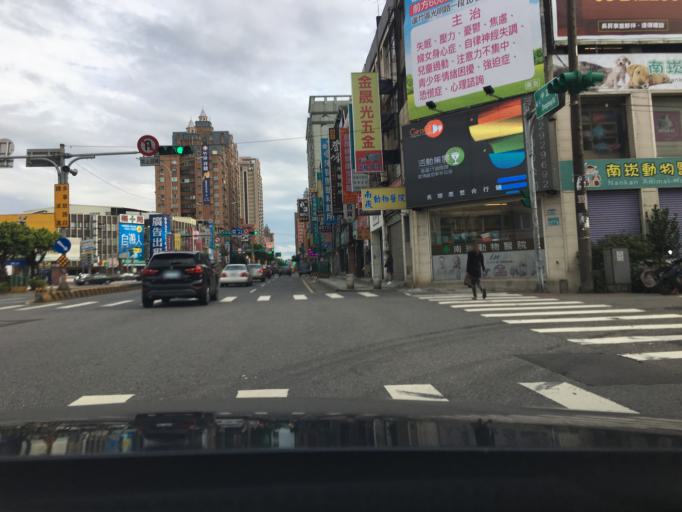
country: TW
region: Taiwan
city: Taoyuan City
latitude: 25.0497
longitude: 121.2907
